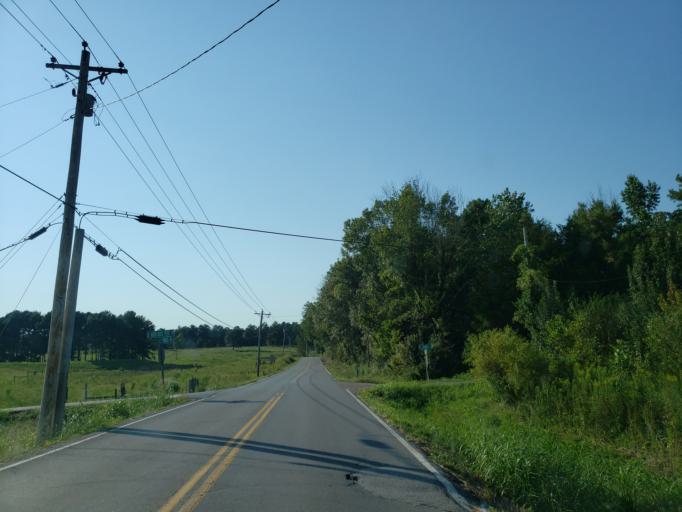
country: US
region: Tennessee
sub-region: Bradley County
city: Wildwood Lake
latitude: 35.0554
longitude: -84.7593
